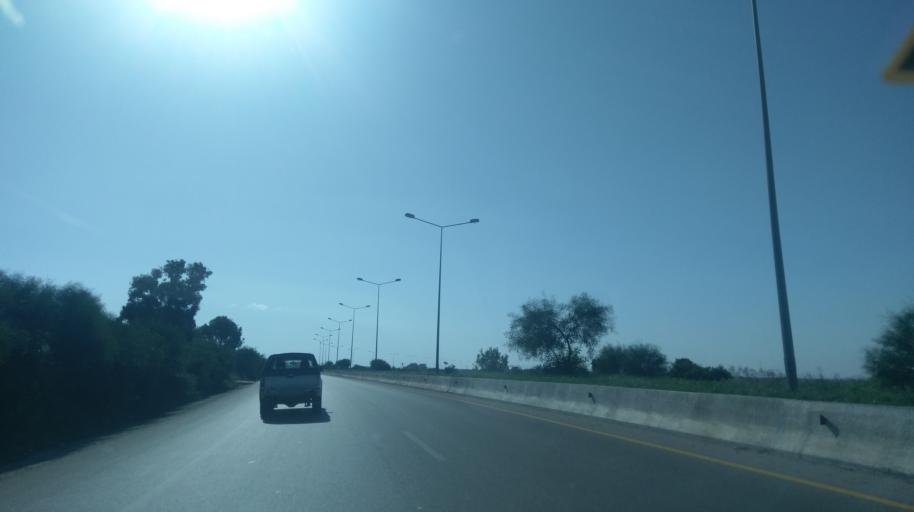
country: CY
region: Ammochostos
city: Trikomo
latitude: 35.2356
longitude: 33.8986
